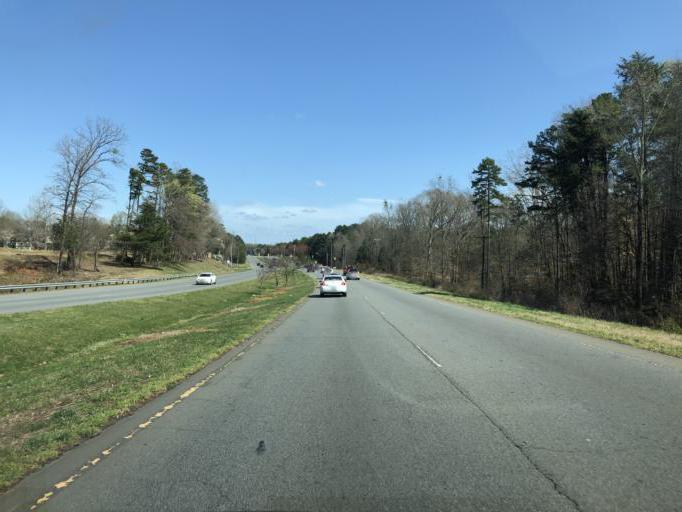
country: US
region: North Carolina
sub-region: Mecklenburg County
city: Huntersville
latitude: 35.3326
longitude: -80.8130
